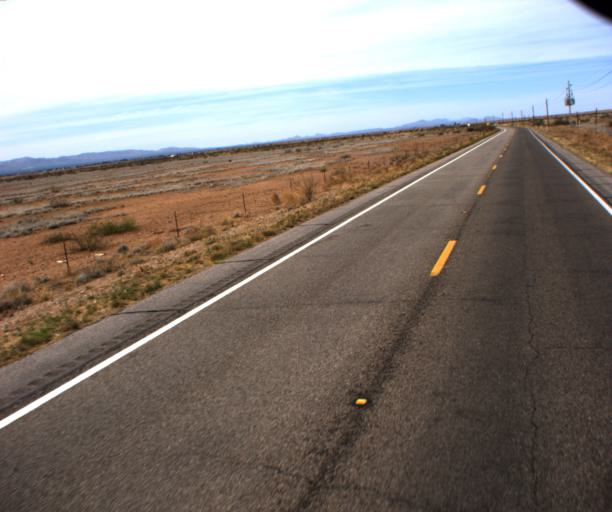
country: US
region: Arizona
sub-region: Cochise County
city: Pirtleville
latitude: 31.4298
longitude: -109.5856
